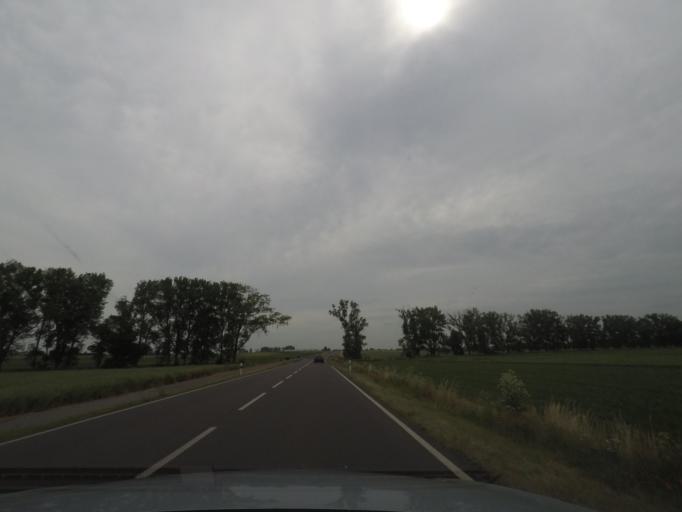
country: DE
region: Saxony-Anhalt
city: Hadmersleben
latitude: 52.0144
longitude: 11.3159
